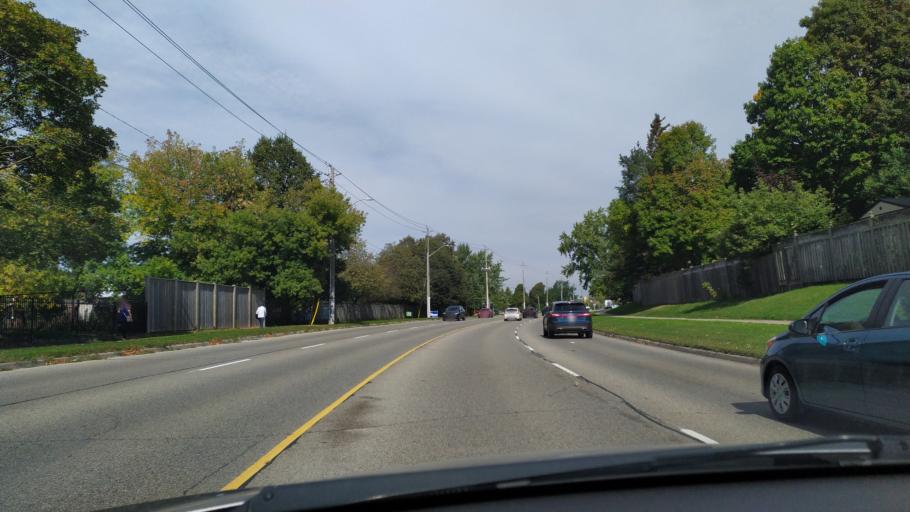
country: CA
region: Ontario
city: Kitchener
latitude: 43.4408
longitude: -80.5220
